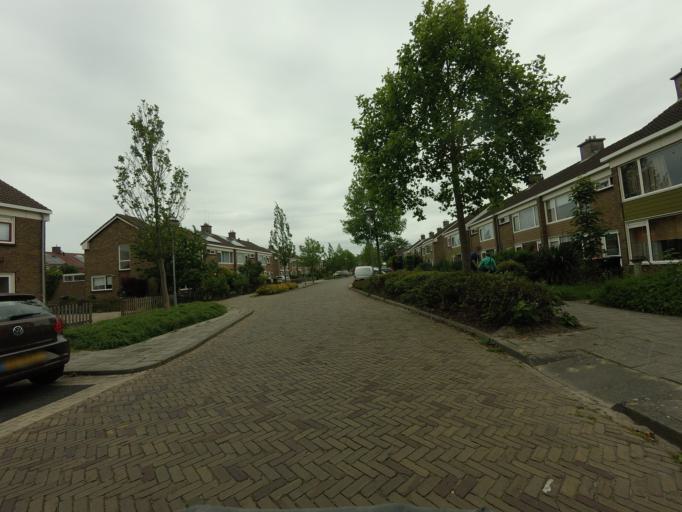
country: NL
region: North Holland
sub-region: Gemeente Medemblik
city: Medemblik
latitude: 52.7672
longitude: 5.1070
